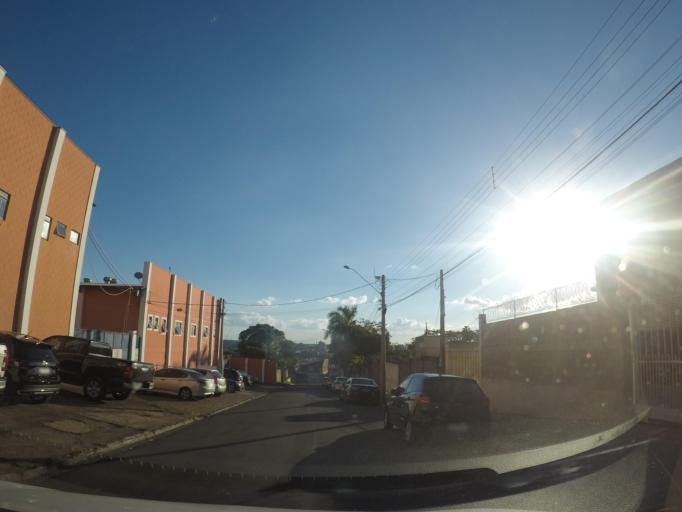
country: BR
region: Sao Paulo
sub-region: Sumare
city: Sumare
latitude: -22.8096
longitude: -47.2492
